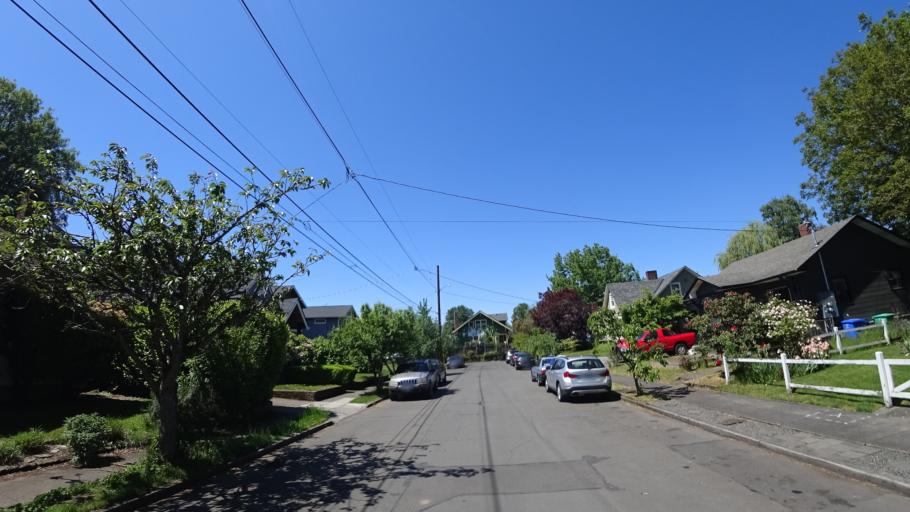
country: US
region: Oregon
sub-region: Multnomah County
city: Portland
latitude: 45.5055
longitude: -122.6263
